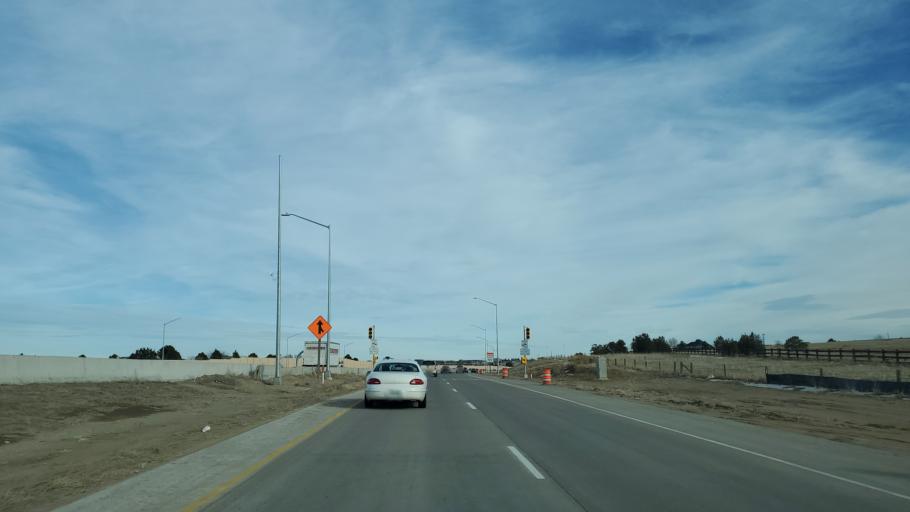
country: US
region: Colorado
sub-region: Douglas County
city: Highlands Ranch
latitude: 39.5630
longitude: -104.9576
